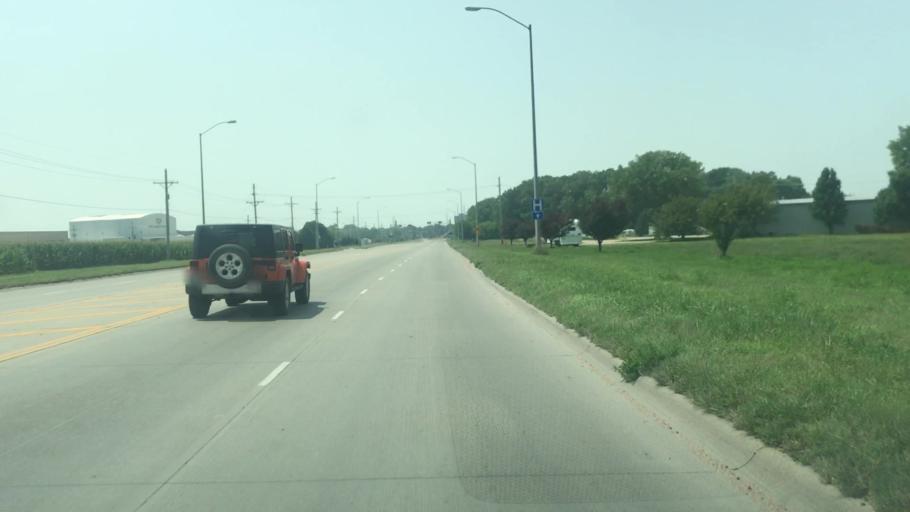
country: US
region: Nebraska
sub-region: Hall County
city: Grand Island
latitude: 40.9303
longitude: -98.3231
